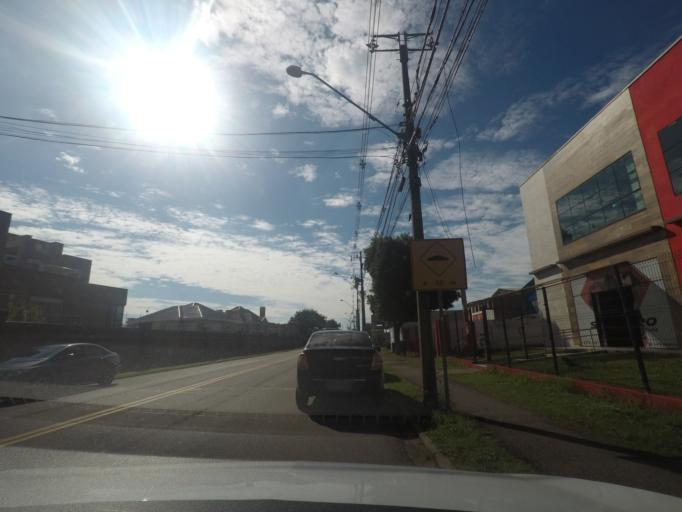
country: BR
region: Parana
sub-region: Curitiba
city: Curitiba
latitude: -25.4954
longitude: -49.2678
